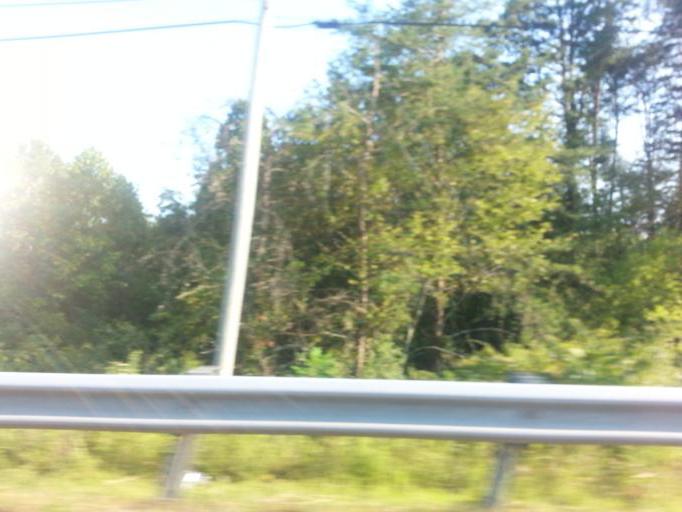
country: US
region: Tennessee
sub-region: Knox County
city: Knoxville
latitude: 35.9001
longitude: -83.8644
